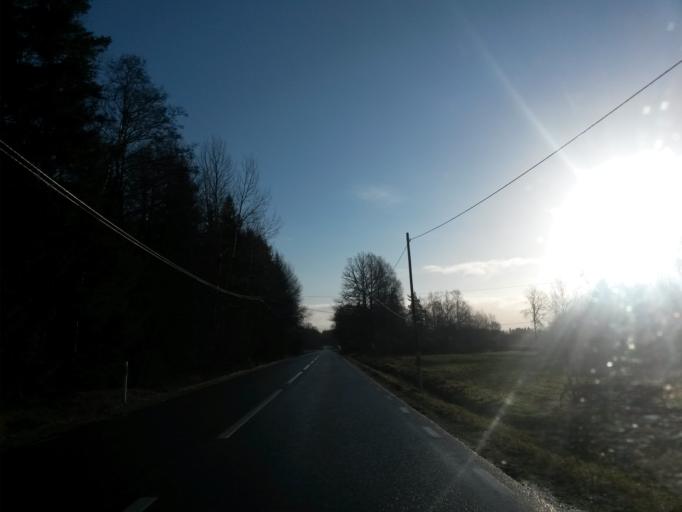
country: SE
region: Vaestra Goetaland
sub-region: Vargarda Kommun
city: Vargarda
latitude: 57.9339
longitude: 12.8537
